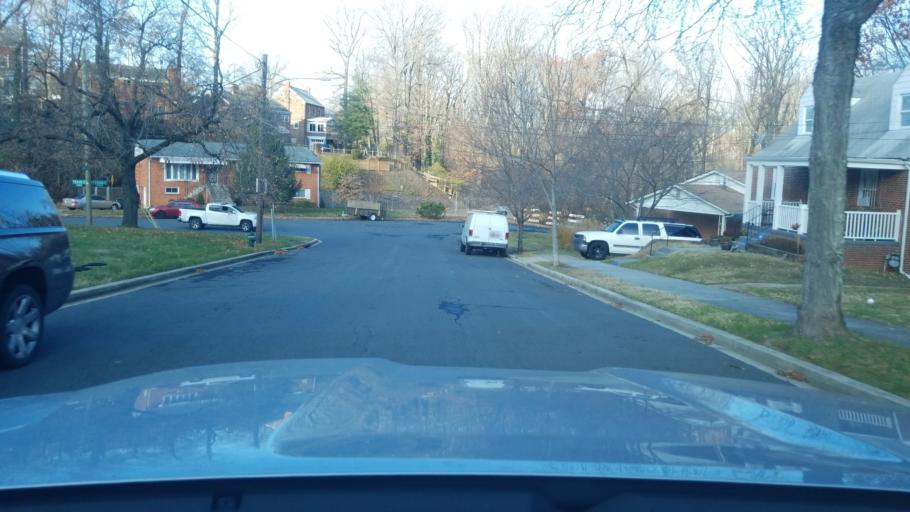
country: US
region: Maryland
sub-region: Prince George's County
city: Coral Hills
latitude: 38.8720
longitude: -76.9517
